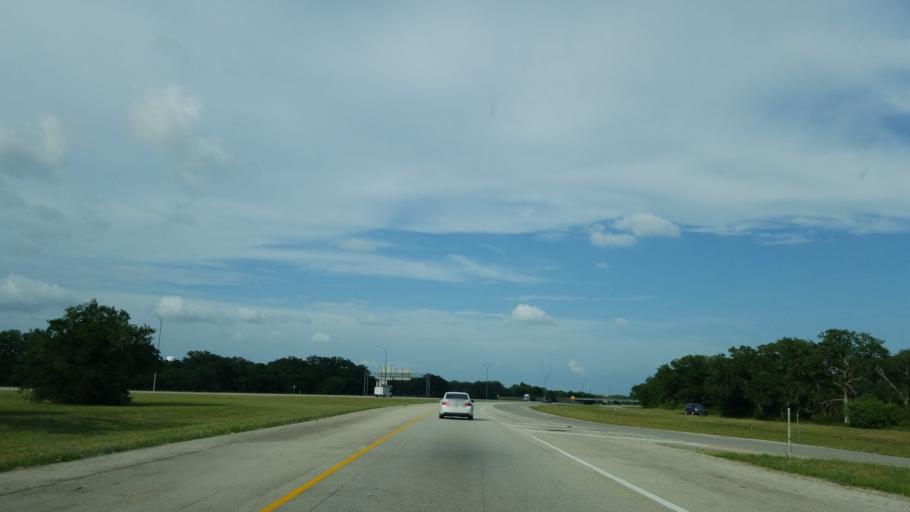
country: US
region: Texas
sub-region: Colorado County
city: Columbus
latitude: 29.6927
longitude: -96.5694
